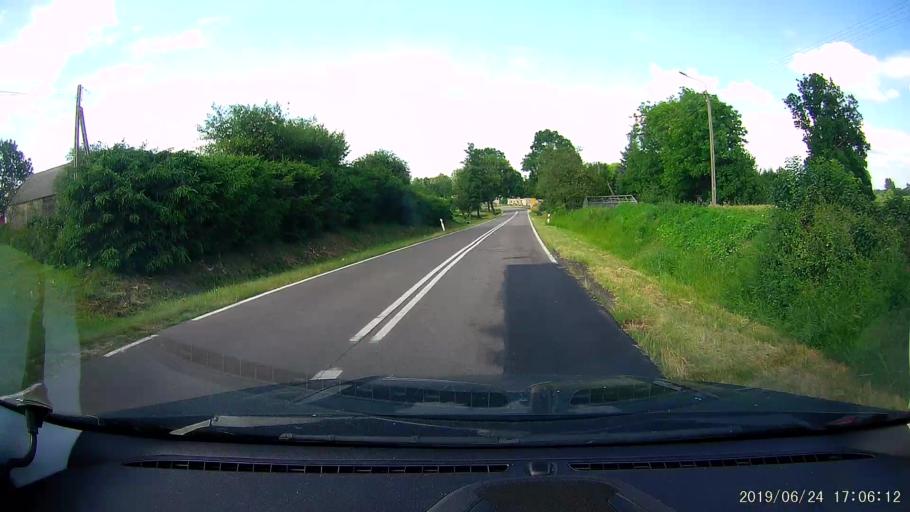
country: PL
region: Lublin Voivodeship
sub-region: Powiat hrubieszowski
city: Dolhobyczow
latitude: 50.5846
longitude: 23.9700
